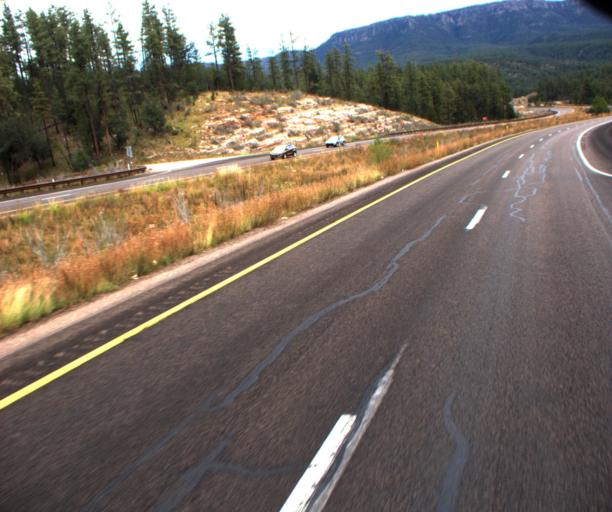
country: US
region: Arizona
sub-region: Gila County
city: Star Valley
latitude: 34.3233
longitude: -111.1108
